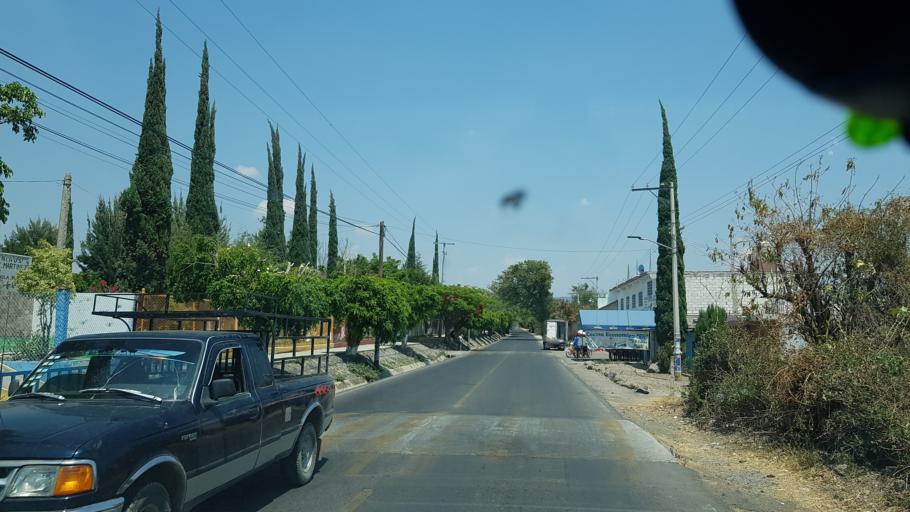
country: MX
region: Puebla
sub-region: Huaquechula
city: Cacaloxuchitl
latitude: 18.7872
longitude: -98.4816
